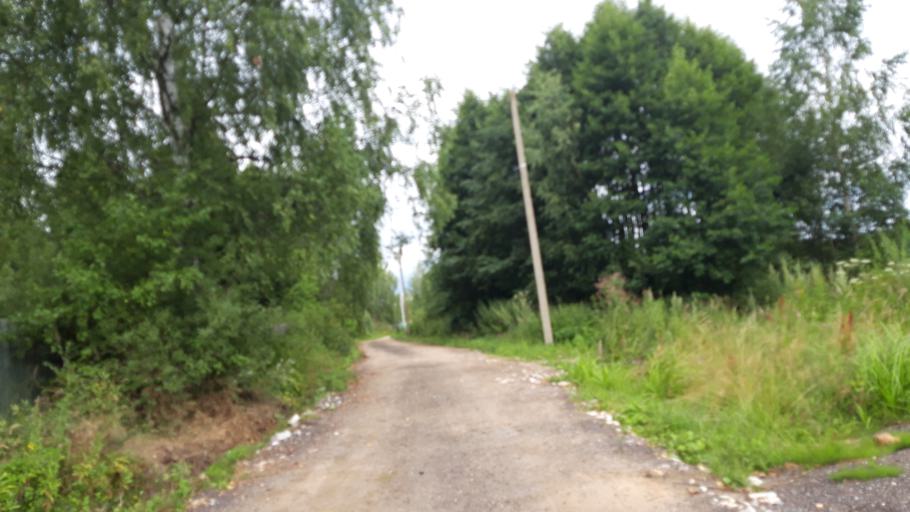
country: RU
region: Tverskaya
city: Konakovo
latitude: 56.6731
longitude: 36.7219
